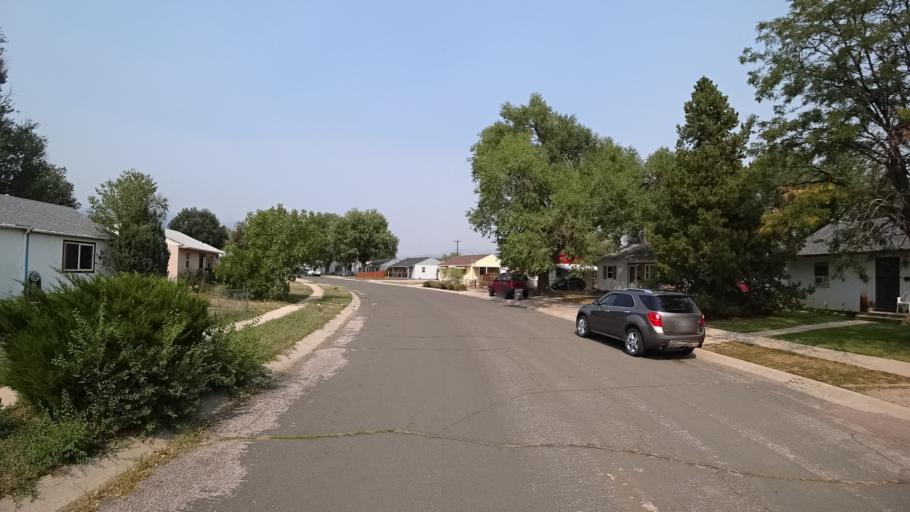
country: US
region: Colorado
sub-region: El Paso County
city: Colorado Springs
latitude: 38.8098
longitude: -104.8138
